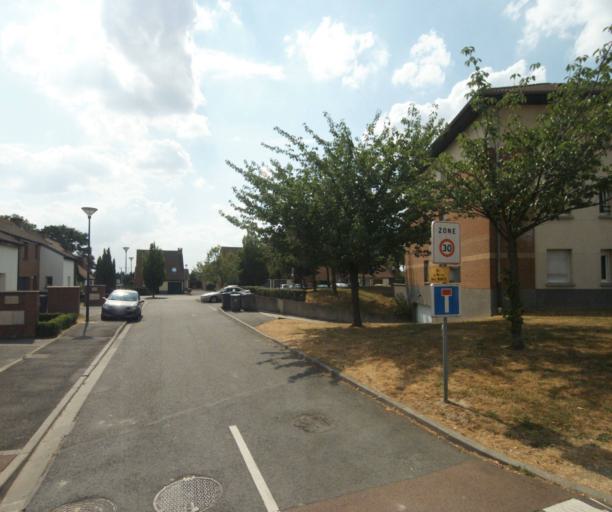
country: FR
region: Nord-Pas-de-Calais
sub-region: Departement du Nord
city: Neuville-en-Ferrain
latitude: 50.7429
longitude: 3.1634
